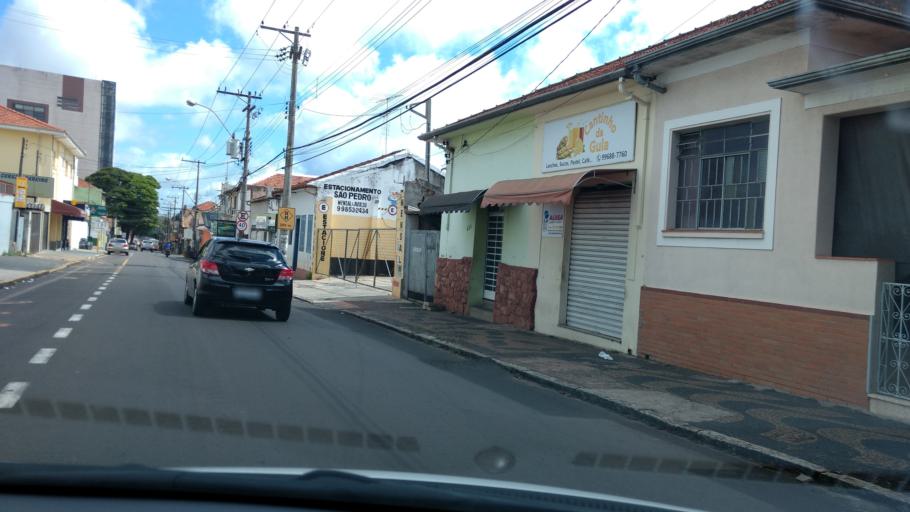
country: BR
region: Sao Paulo
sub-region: Botucatu
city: Botucatu
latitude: -22.8876
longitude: -48.4400
